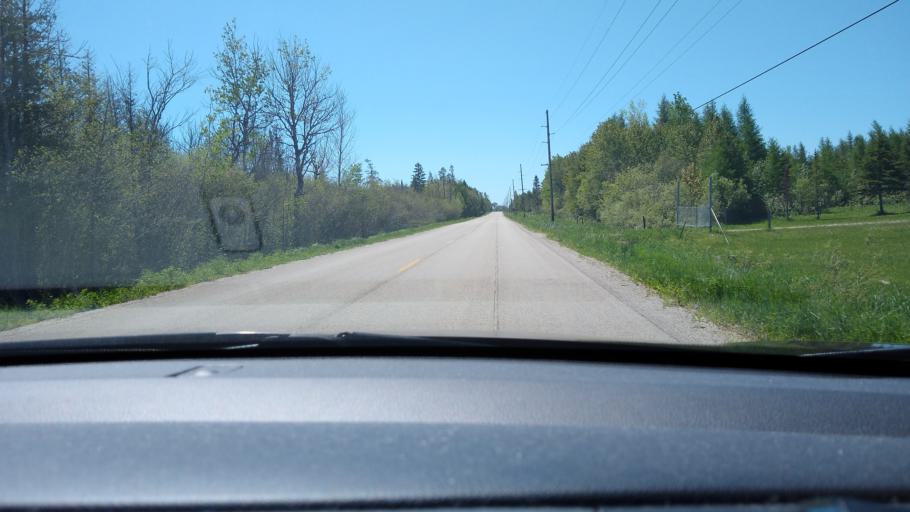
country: US
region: Michigan
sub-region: Delta County
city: Gladstone
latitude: 45.8553
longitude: -87.1841
